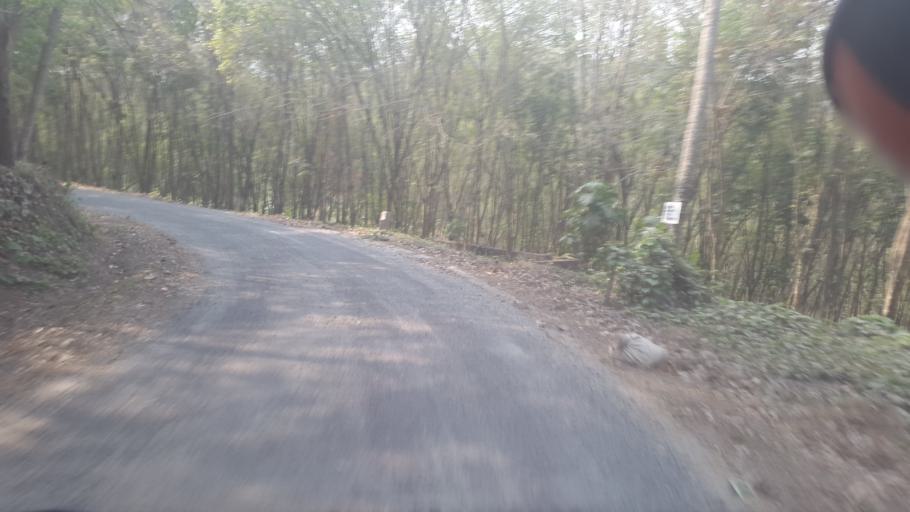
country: ID
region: West Java
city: Pelabuhanratu
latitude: -6.9586
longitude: 106.5311
